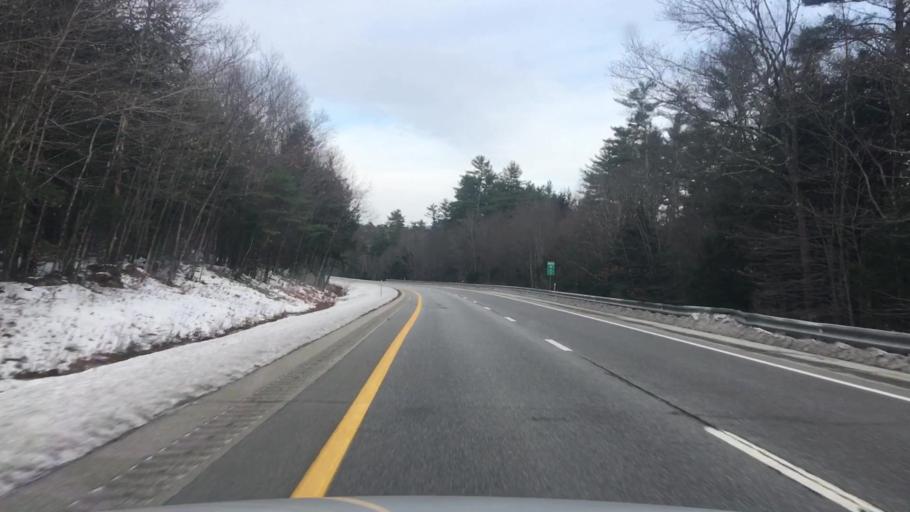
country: US
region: New Hampshire
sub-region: Merrimack County
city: Sutton
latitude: 43.3082
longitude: -71.8439
